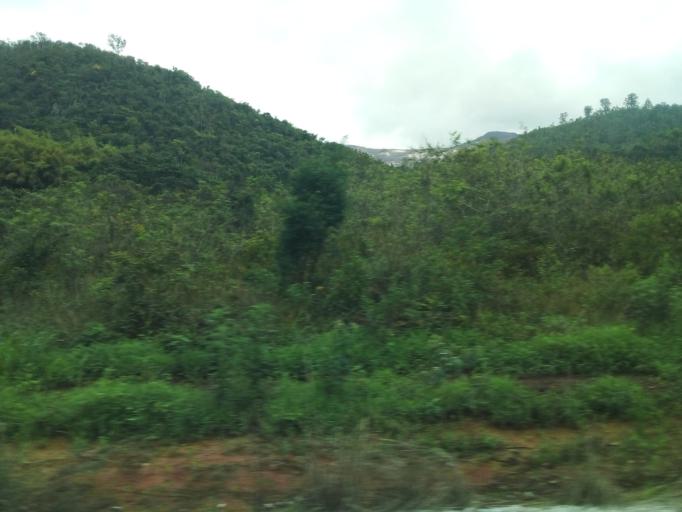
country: BR
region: Minas Gerais
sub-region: Rio Piracicaba
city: Rio Piracicaba
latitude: -19.9740
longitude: -43.2376
